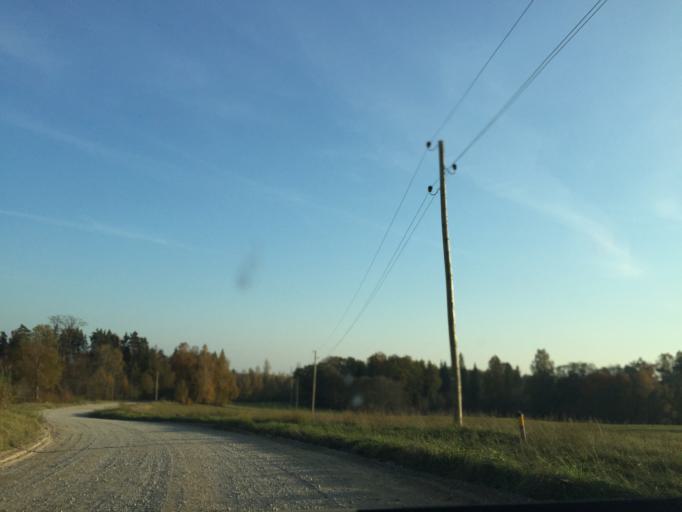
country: LV
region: Vainode
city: Vainode
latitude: 56.6067
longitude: 21.8233
